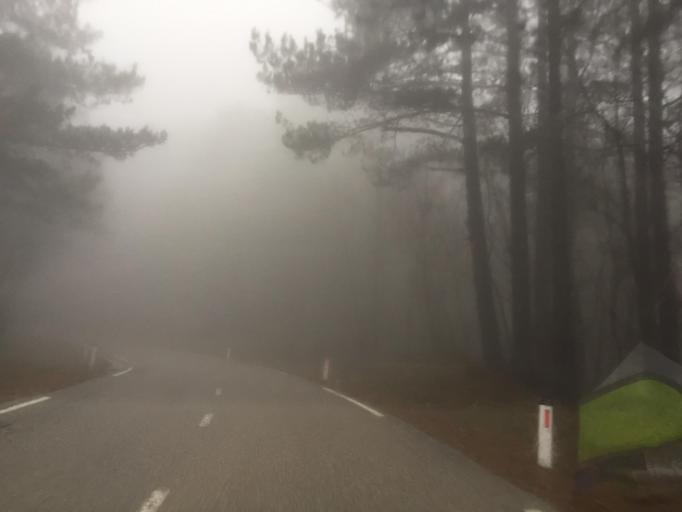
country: SI
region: Ajdovscina
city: Lokavec
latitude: 45.9296
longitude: 13.8732
